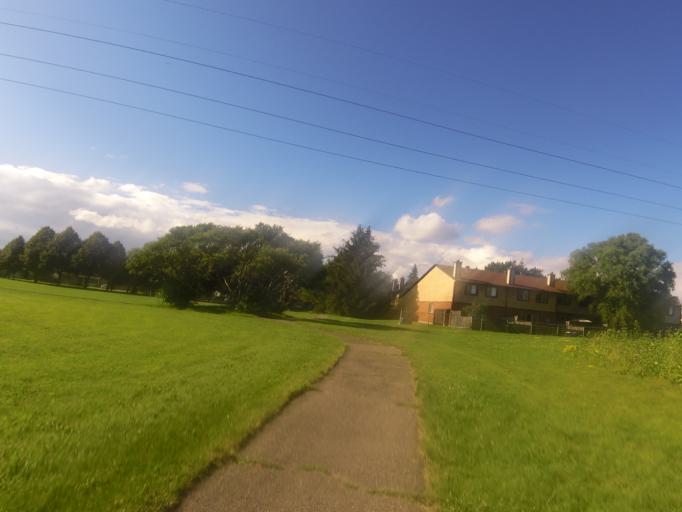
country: CA
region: Ontario
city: Ottawa
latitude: 45.3353
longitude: -75.7433
